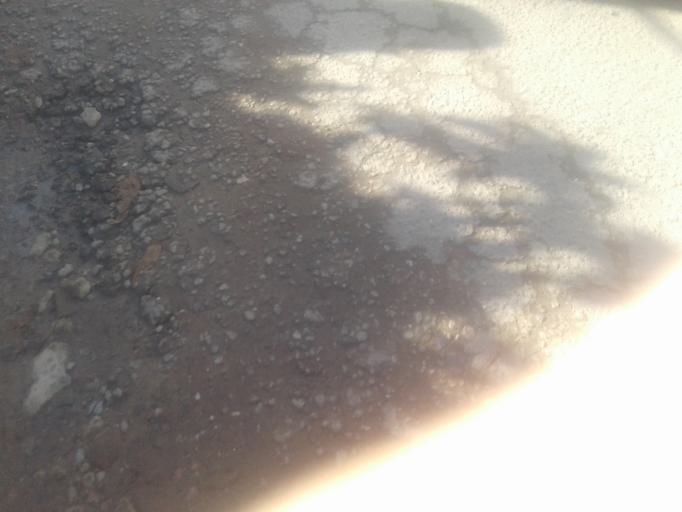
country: AR
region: Buenos Aires F.D.
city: Villa Lugano
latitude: -34.6726
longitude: -58.4684
